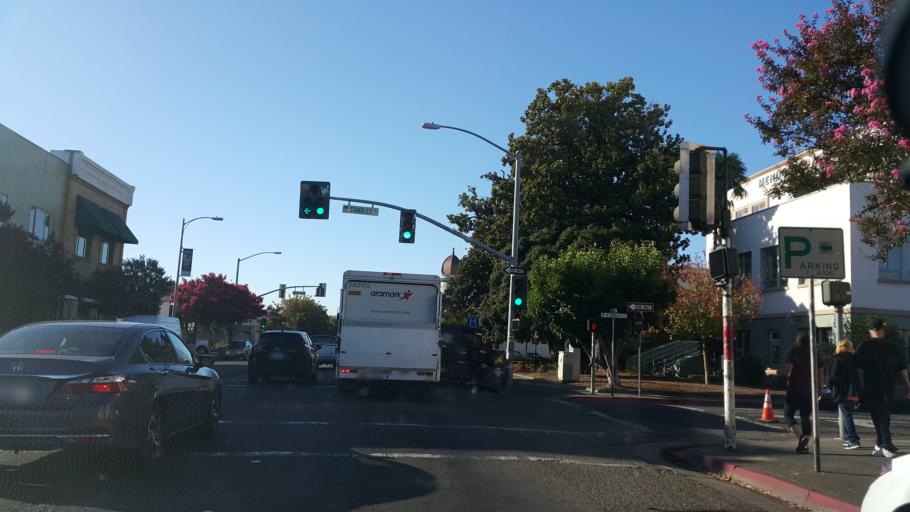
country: US
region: California
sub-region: Mendocino County
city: Ukiah
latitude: 39.1510
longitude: -123.2079
